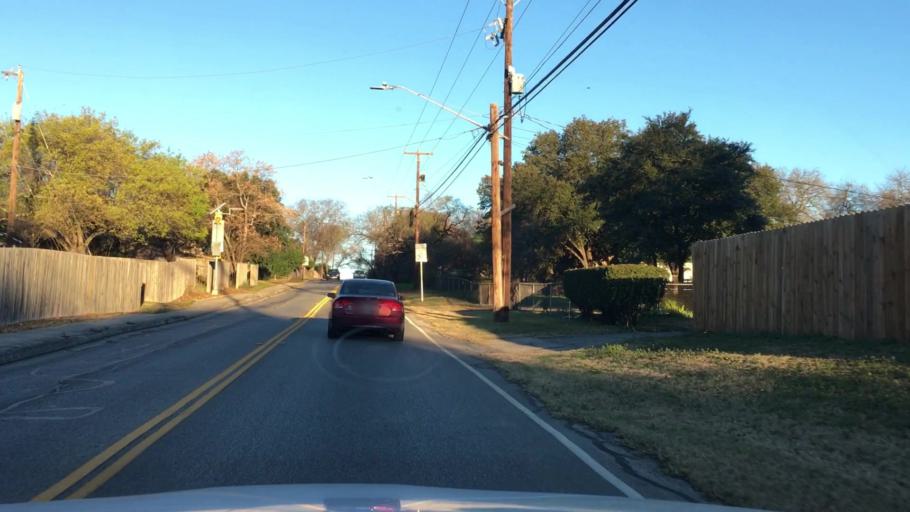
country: US
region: Texas
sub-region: Bexar County
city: Castle Hills
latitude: 29.5351
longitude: -98.5015
